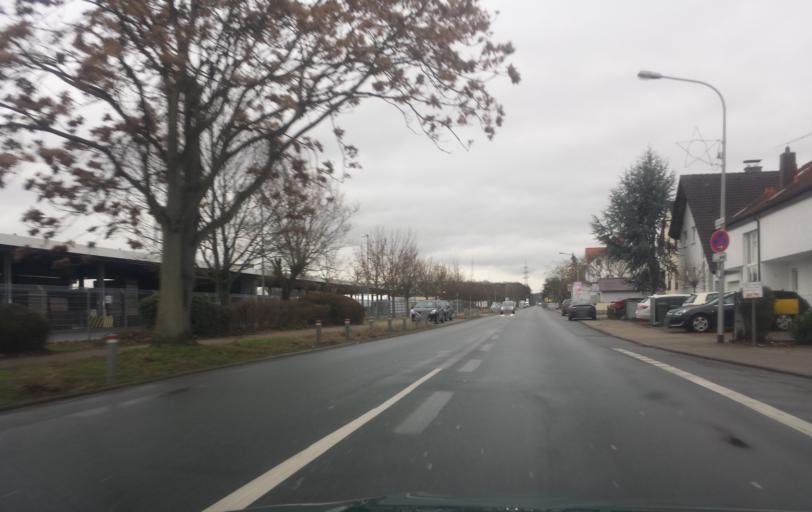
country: DE
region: Hesse
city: Weiterstadt
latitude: 49.8925
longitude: 8.6121
